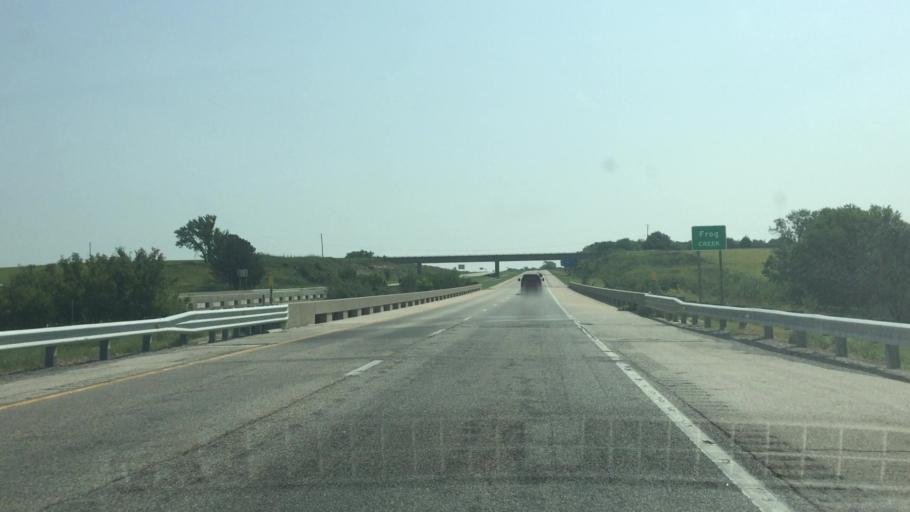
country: US
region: Kansas
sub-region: Osage County
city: Lyndon
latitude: 38.4261
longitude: -95.7512
